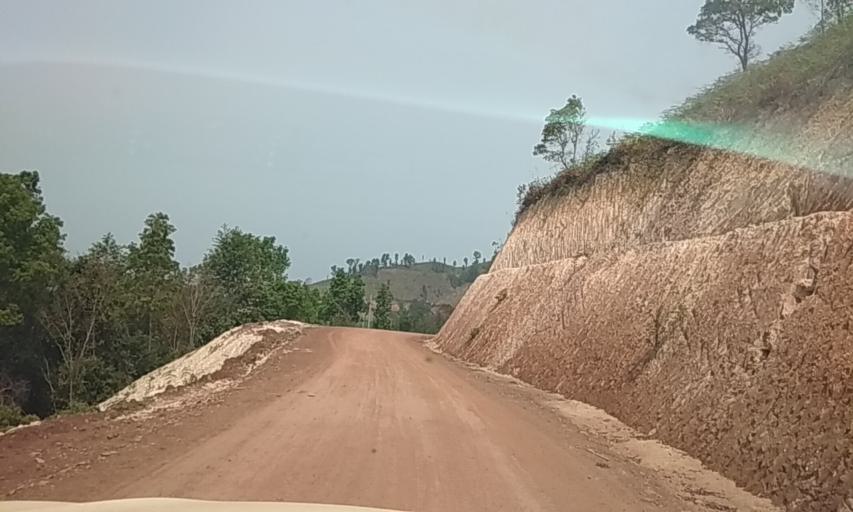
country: VN
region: Huyen Dien Bien
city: Dien Bien Phu
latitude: 21.4780
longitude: 102.7798
